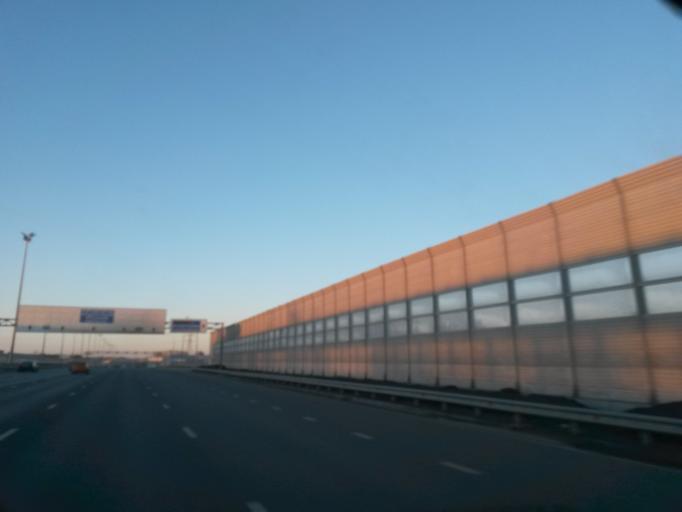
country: RU
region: Moskovskaya
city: Bolshevo
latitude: 55.9579
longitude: 37.8324
